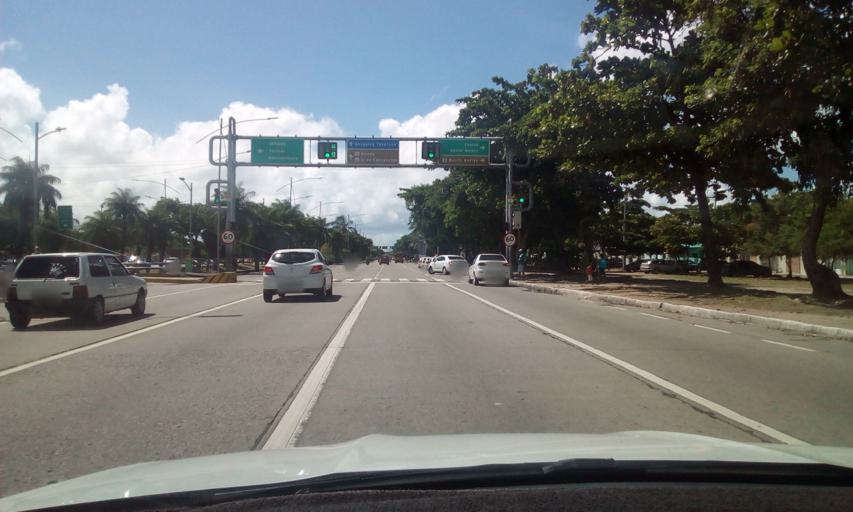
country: BR
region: Pernambuco
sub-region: Recife
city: Recife
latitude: -8.0414
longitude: -34.8820
